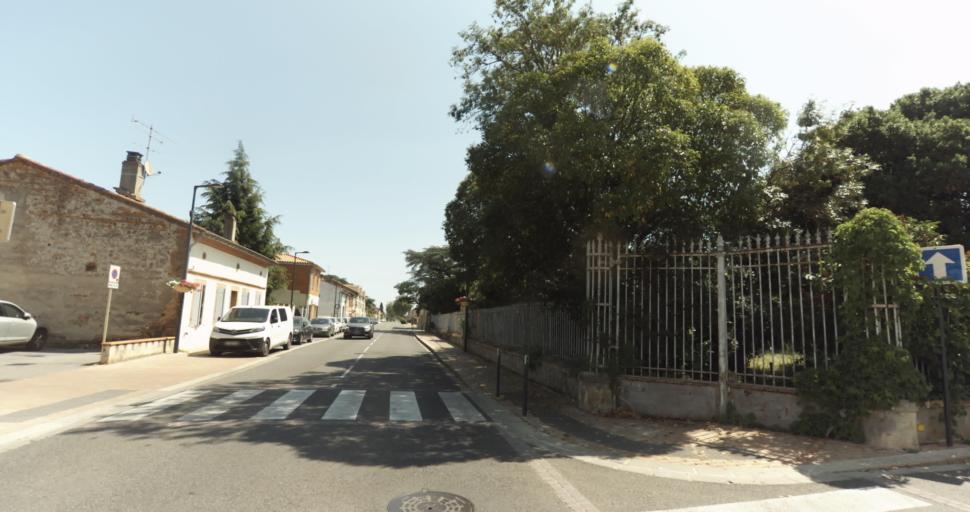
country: FR
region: Midi-Pyrenees
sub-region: Departement de la Haute-Garonne
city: Plaisance-du-Touch
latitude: 43.5663
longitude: 1.2986
